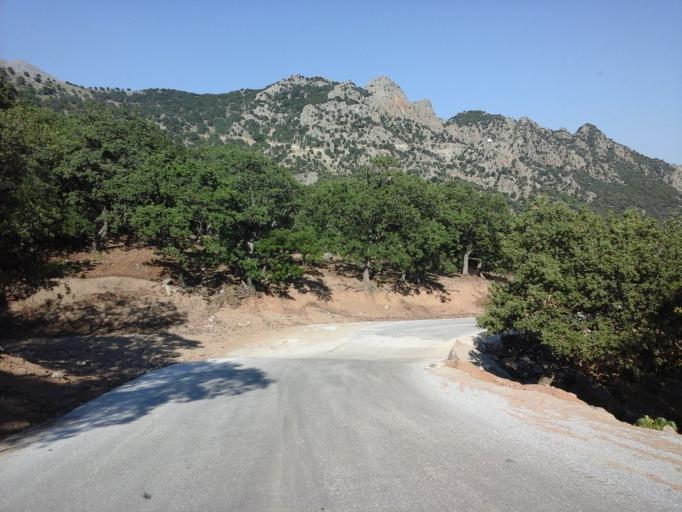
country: GR
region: East Macedonia and Thrace
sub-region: Nomos Evrou
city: Samothraki
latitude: 40.4083
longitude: 25.5721
